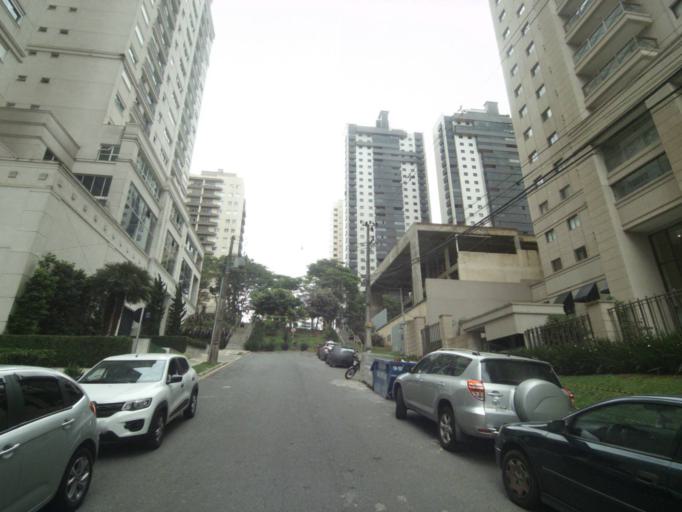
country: BR
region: Parana
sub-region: Curitiba
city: Curitiba
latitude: -25.4335
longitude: -49.3024
